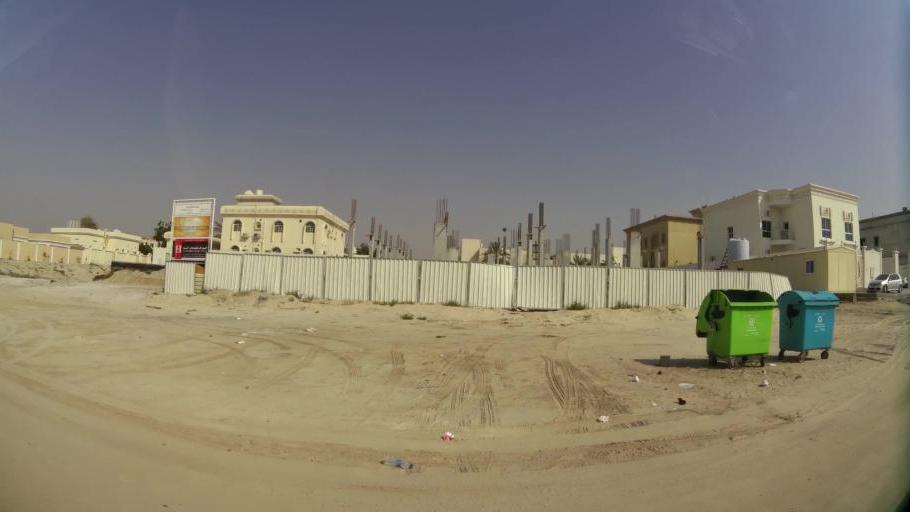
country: AE
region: Ajman
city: Ajman
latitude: 25.3879
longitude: 55.4281
